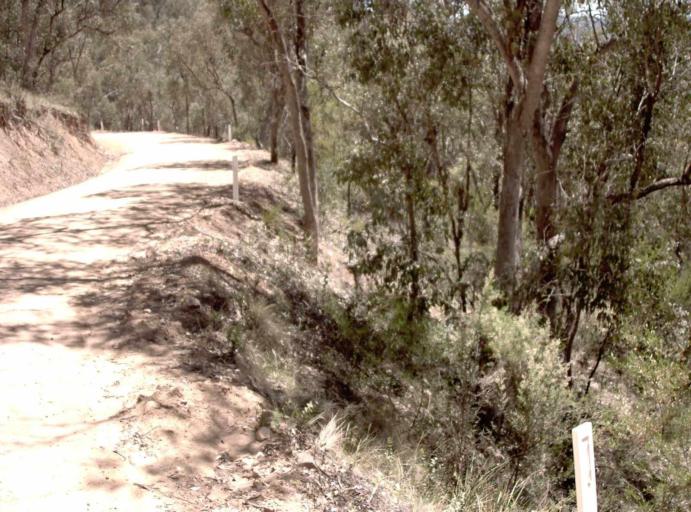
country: AU
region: New South Wales
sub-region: Snowy River
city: Jindabyne
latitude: -36.9783
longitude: 148.3013
